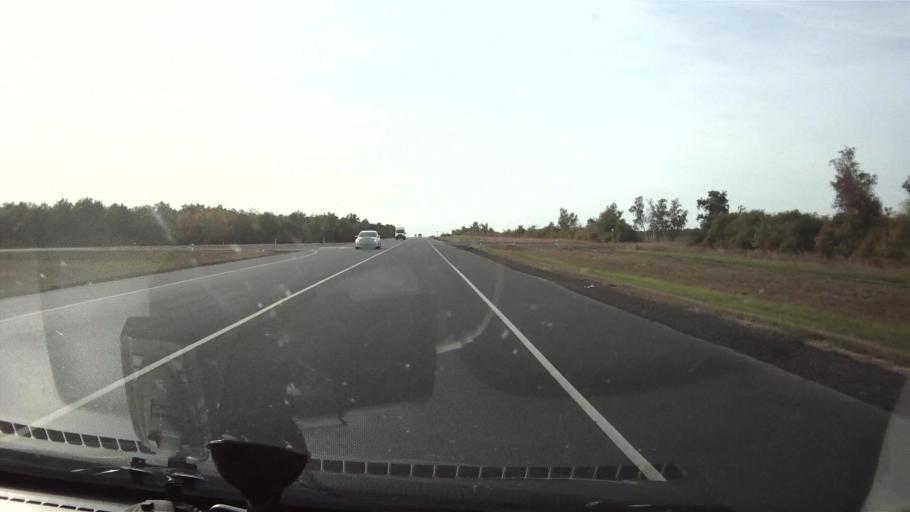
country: RU
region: Saratov
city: Yelshanka
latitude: 51.8202
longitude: 46.3488
